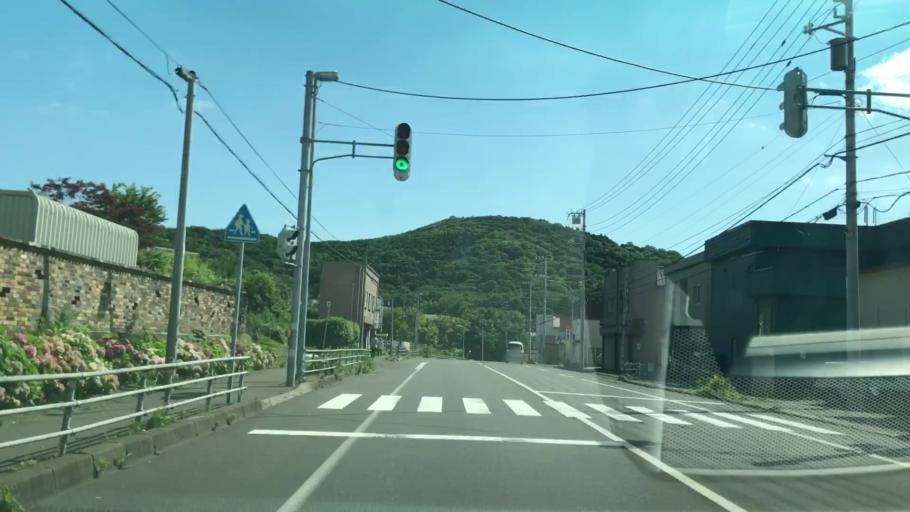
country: JP
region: Hokkaido
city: Muroran
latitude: 42.3222
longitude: 140.9969
